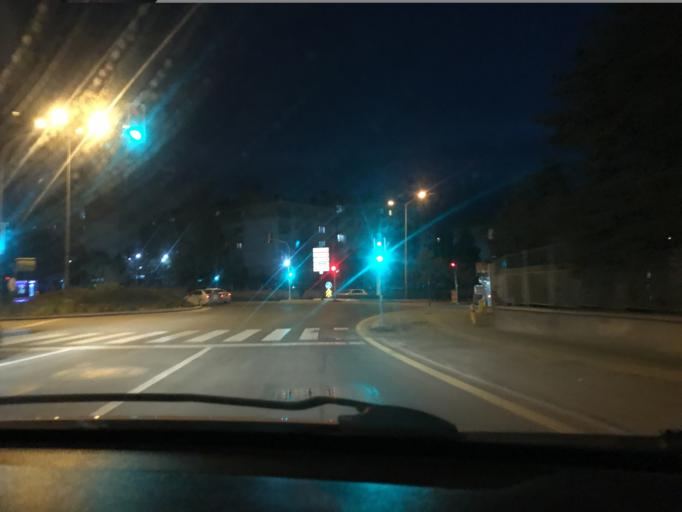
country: TR
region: Ankara
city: Batikent
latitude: 39.9585
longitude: 32.7293
